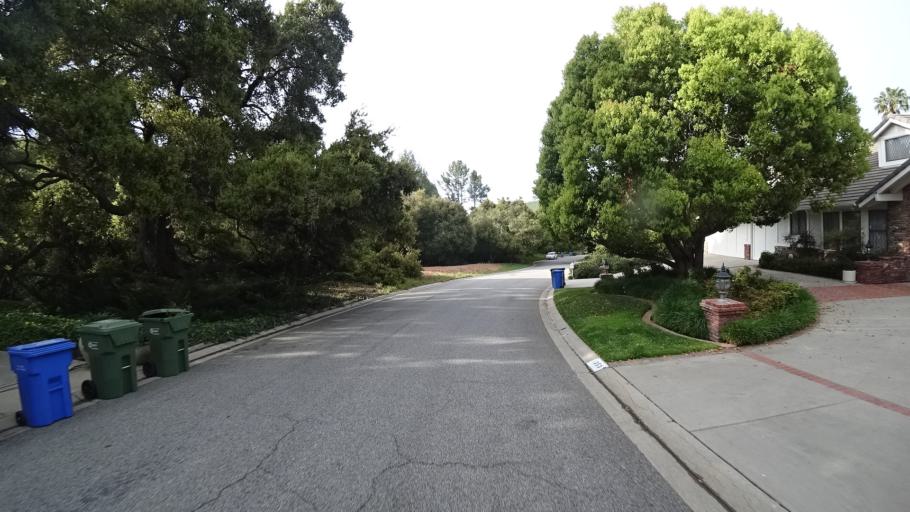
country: US
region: California
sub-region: Ventura County
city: Thousand Oaks
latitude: 34.1885
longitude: -118.8201
